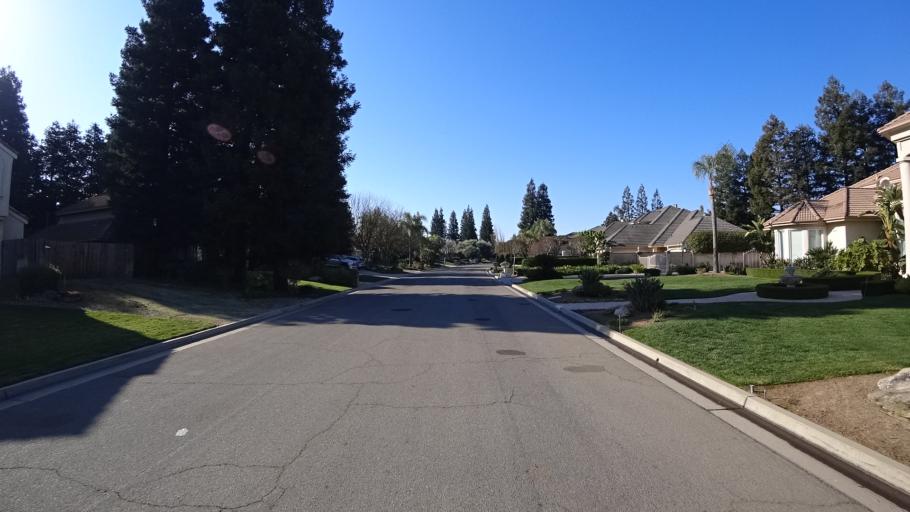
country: US
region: California
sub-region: Fresno County
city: Clovis
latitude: 36.8645
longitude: -119.7960
